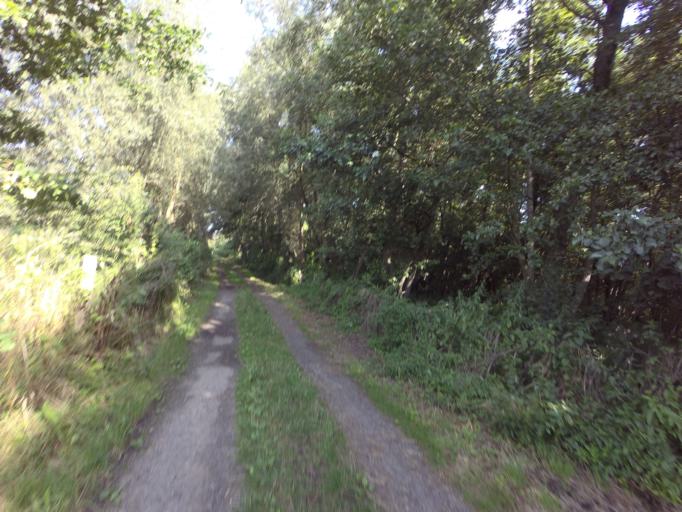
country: BE
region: Wallonia
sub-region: Province de Liege
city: Plombieres
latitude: 50.7497
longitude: 5.9439
